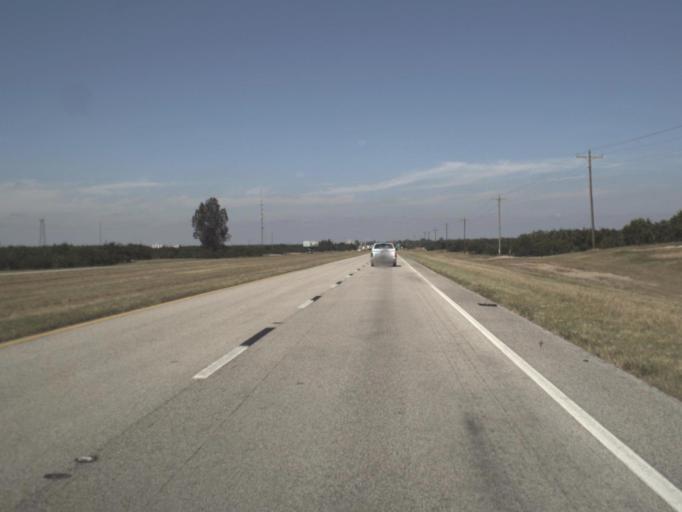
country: US
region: Florida
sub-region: Highlands County
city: Placid Lakes
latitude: 27.1923
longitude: -81.3285
